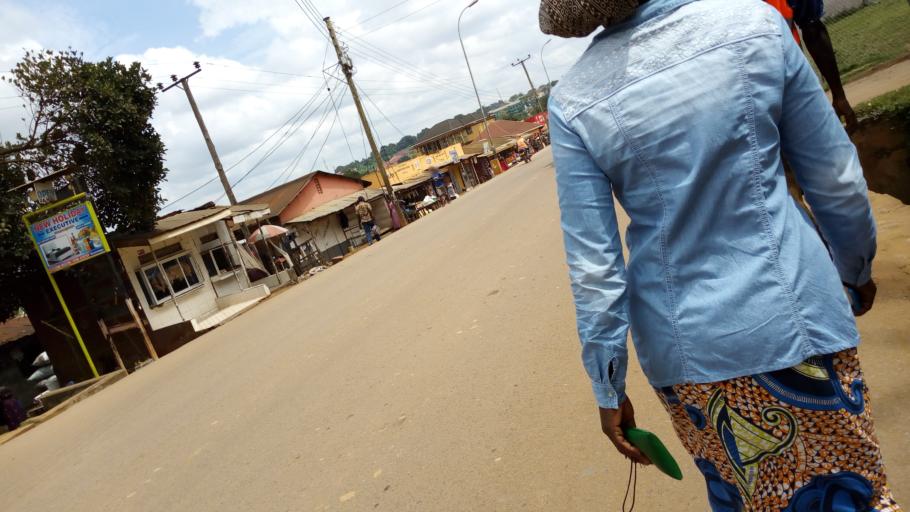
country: UG
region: Central Region
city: Kampala Central Division
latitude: 0.3809
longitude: 32.5594
